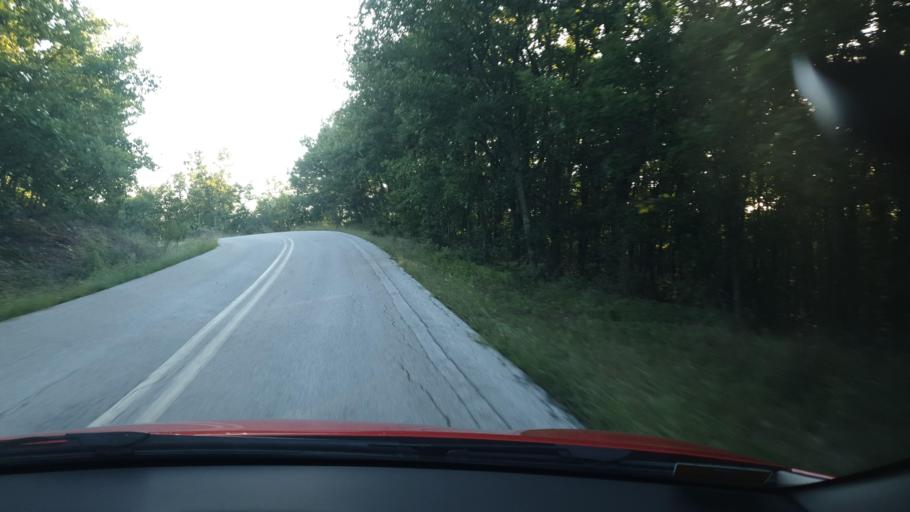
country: GR
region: Central Macedonia
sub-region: Nomos Chalkidikis
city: Galatista
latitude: 40.5366
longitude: 23.2773
